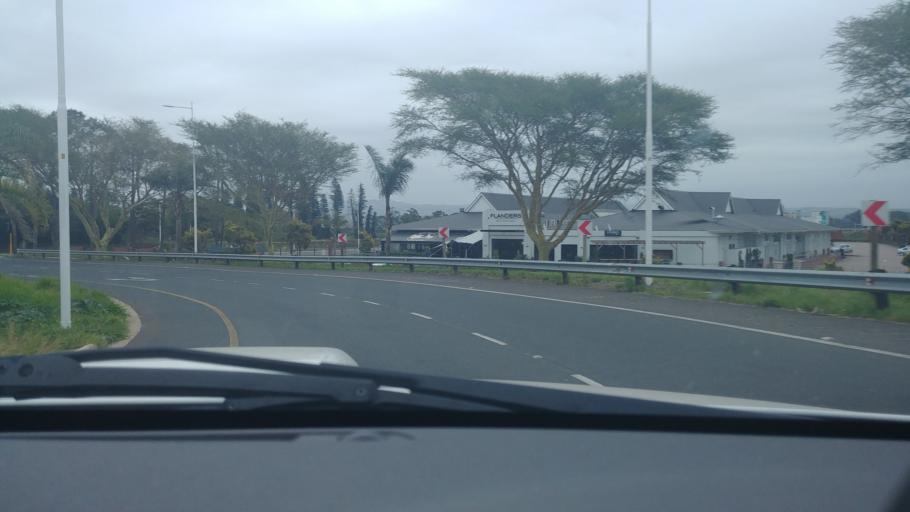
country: ZA
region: KwaZulu-Natal
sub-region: eThekwini Metropolitan Municipality
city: Durban
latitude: -29.7140
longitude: 31.0530
